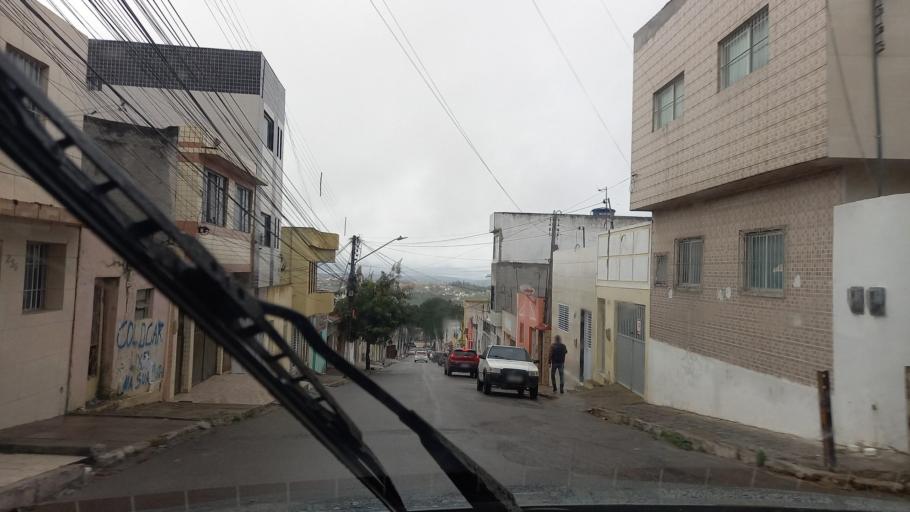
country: BR
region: Pernambuco
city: Garanhuns
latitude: -8.8857
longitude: -36.4939
